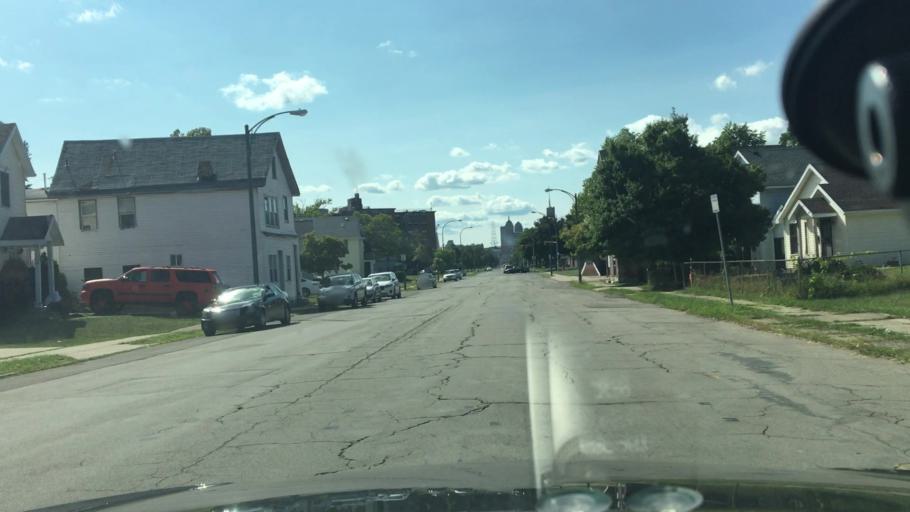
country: US
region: New York
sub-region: Erie County
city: Buffalo
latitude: 42.8816
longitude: -78.8520
